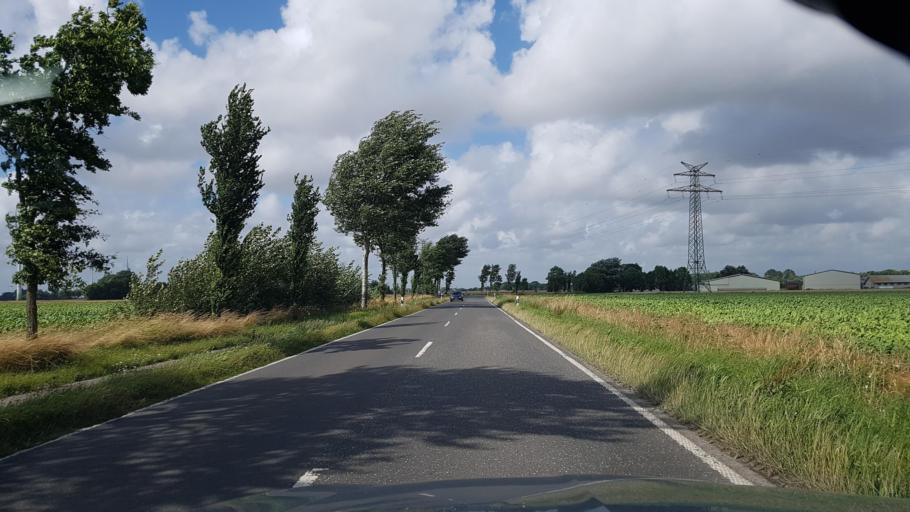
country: DE
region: Schleswig-Holstein
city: Reinsbuttel
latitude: 54.1908
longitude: 8.9024
